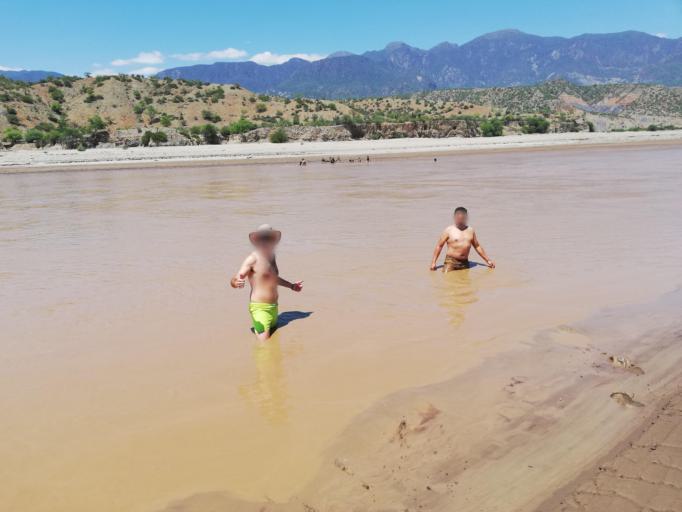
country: BO
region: Chuquisaca
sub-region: Provincia Zudanez
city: Mojocoya
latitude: -18.6752
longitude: -64.5277
